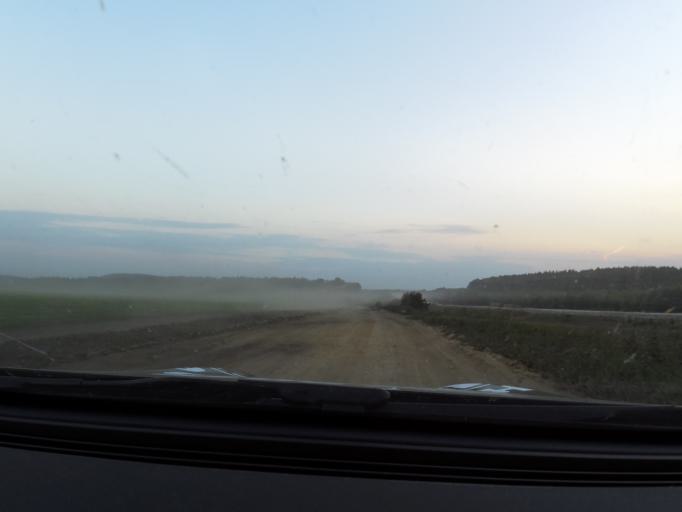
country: RU
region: Sverdlovsk
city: Arti
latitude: 56.3168
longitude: 58.3970
